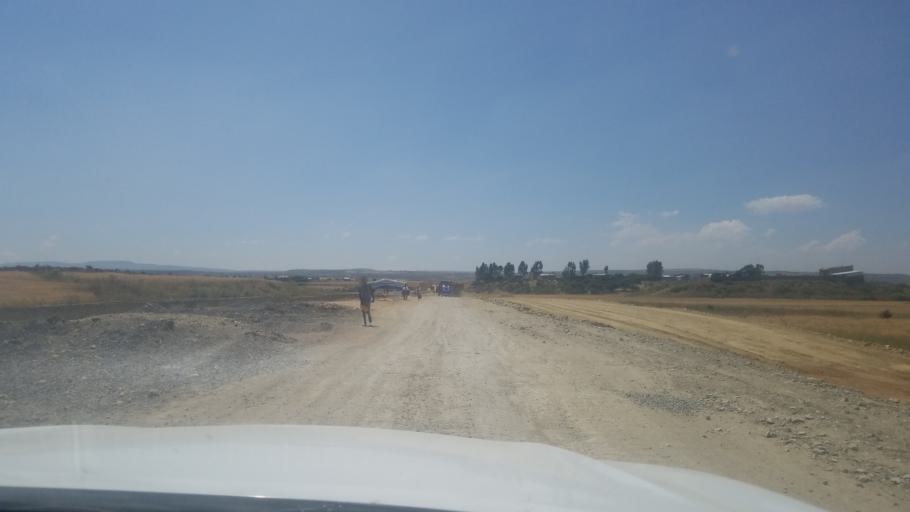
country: ET
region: Tigray
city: Mekele
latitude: 13.7647
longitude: 39.5903
